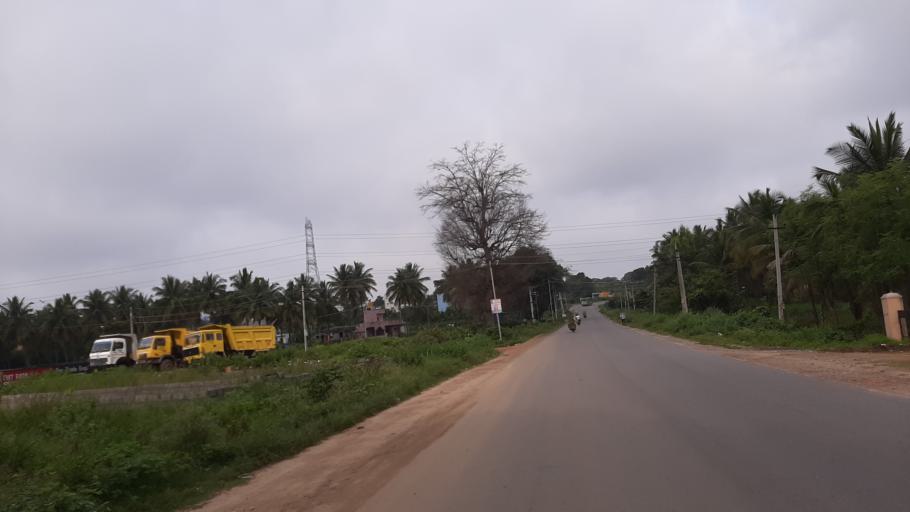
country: IN
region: Karnataka
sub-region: Bangalore Rural
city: Nelamangala
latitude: 12.9651
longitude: 77.3942
